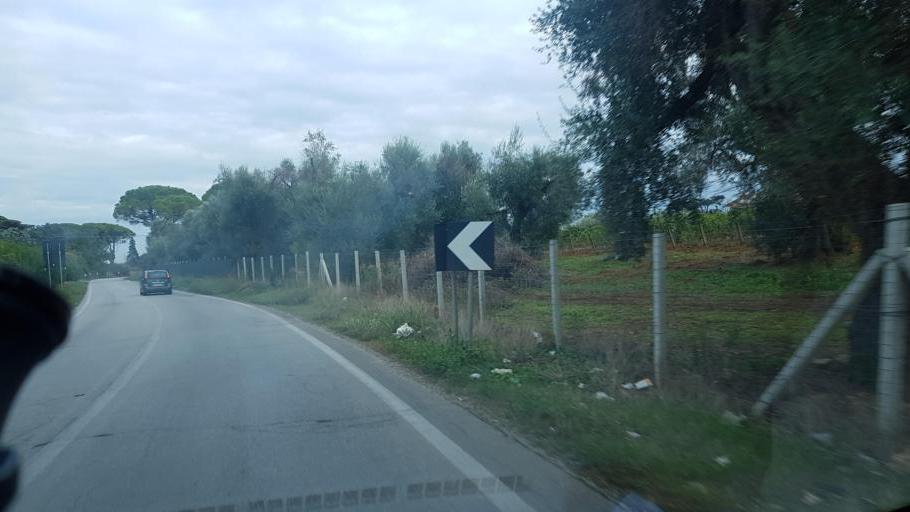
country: IT
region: Apulia
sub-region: Provincia di Brindisi
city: Francavilla Fontana
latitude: 40.5181
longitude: 17.6068
